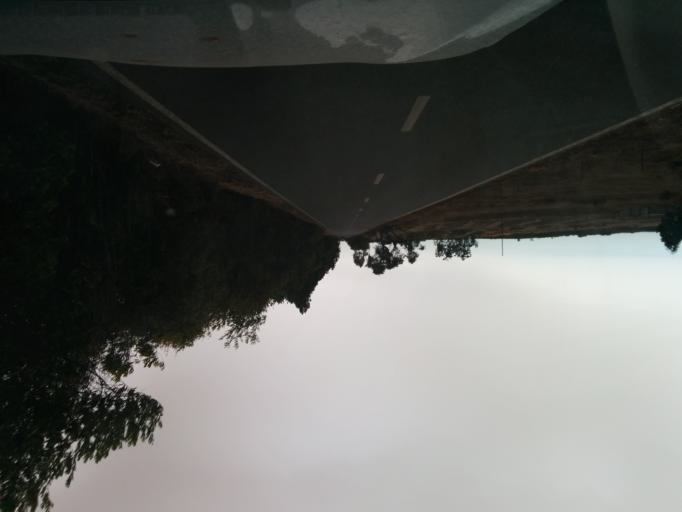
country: PT
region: Beja
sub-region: Odemira
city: Sao Teotonio
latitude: 37.5404
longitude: -8.7504
